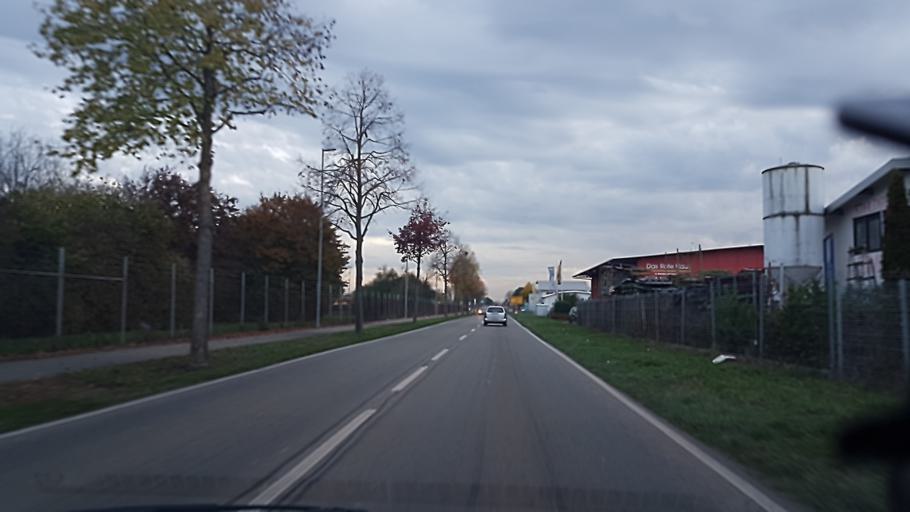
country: DE
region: Baden-Wuerttemberg
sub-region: Freiburg Region
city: Herbolzheim
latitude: 48.2204
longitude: 7.7604
